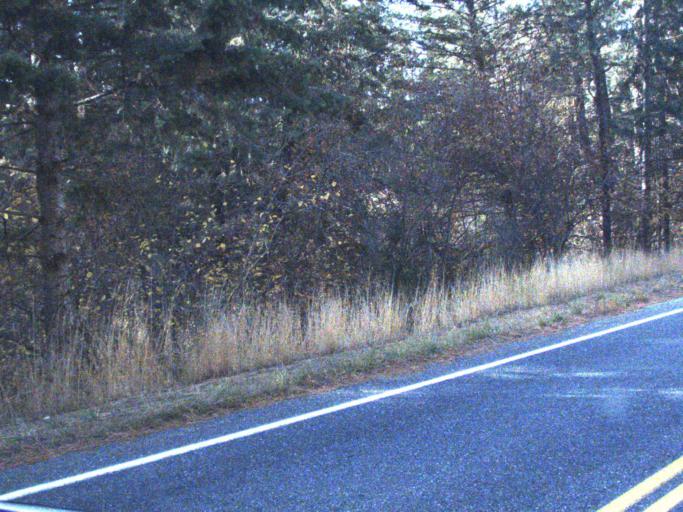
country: US
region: Washington
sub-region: Stevens County
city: Kettle Falls
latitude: 48.4806
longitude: -118.1722
